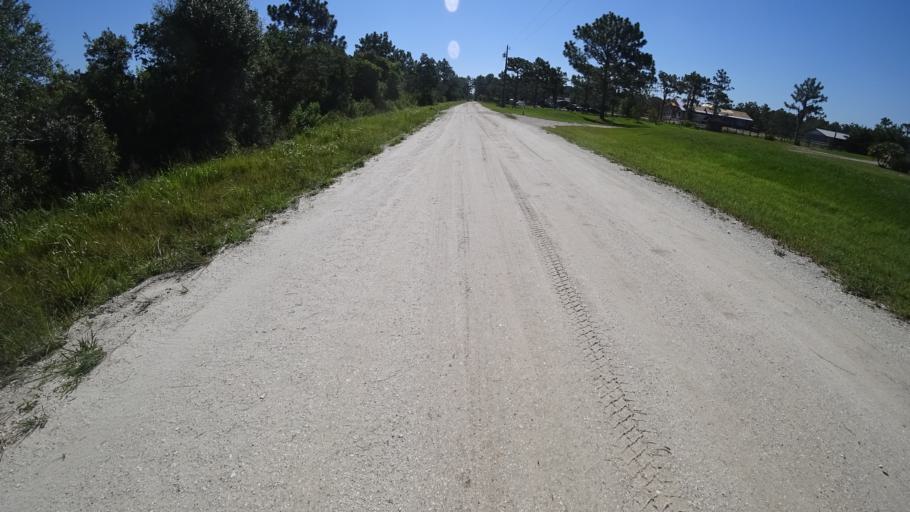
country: US
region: Florida
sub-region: Sarasota County
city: Fruitville
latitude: 27.3979
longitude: -82.2914
